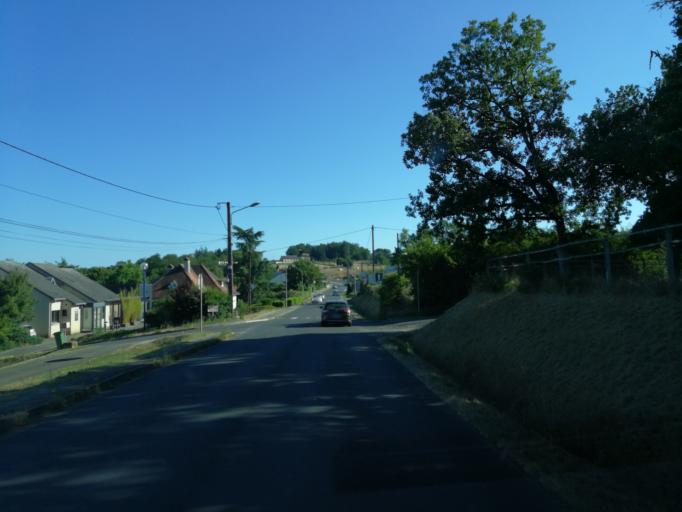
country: FR
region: Midi-Pyrenees
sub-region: Departement du Lot
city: Gourdon
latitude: 44.7287
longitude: 1.3736
